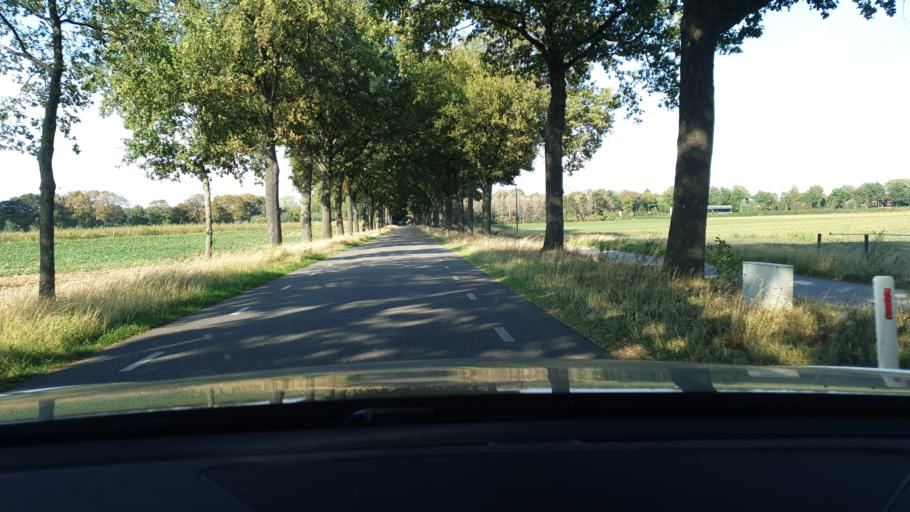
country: NL
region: Limburg
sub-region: Gemeente Maasgouw
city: Maasbracht
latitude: 51.0963
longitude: 5.8625
